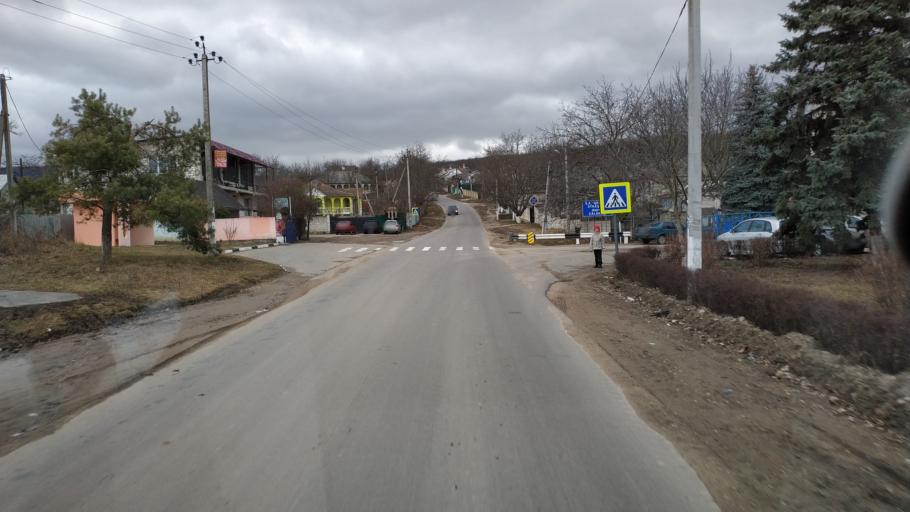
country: MD
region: Calarasi
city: Calarasi
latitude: 47.2450
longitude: 28.2855
